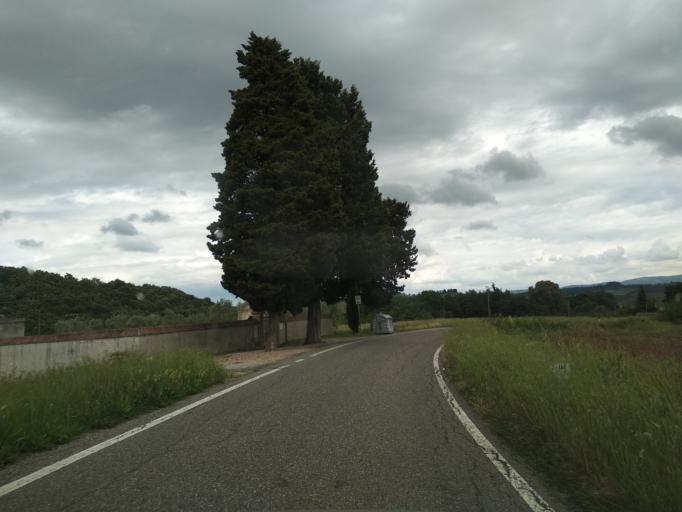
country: IT
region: Tuscany
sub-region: Provincia di Livorno
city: Collesalvetti
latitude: 43.5413
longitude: 10.4506
